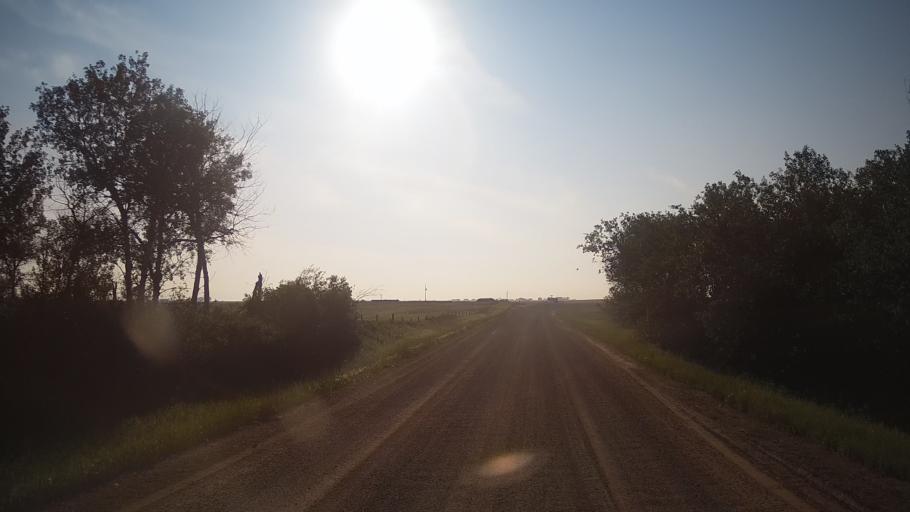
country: CA
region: Saskatchewan
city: Saskatoon
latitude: 51.8237
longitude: -106.5286
